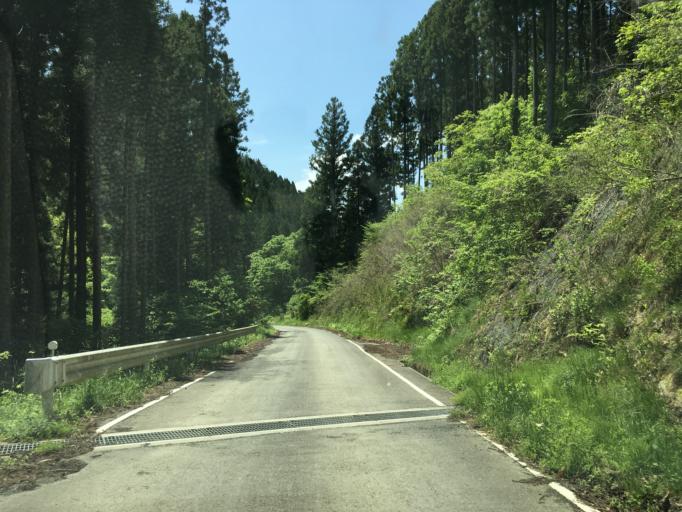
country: JP
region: Miyagi
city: Wakuya
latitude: 38.6875
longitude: 141.3479
